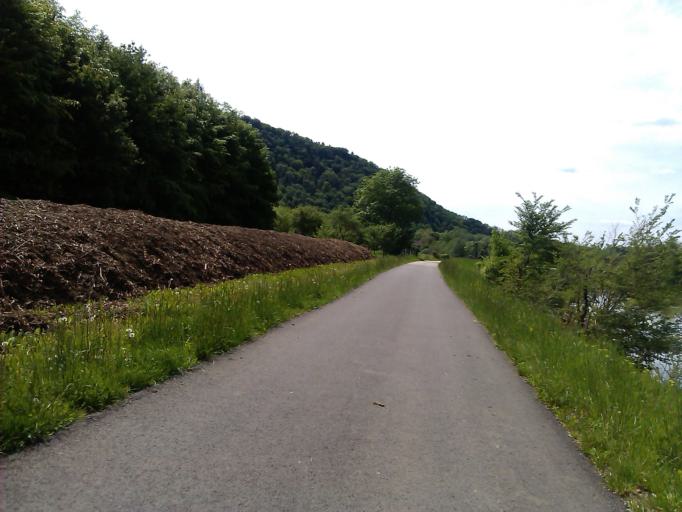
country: FR
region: Franche-Comte
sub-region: Departement du Doubs
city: Montferrand-le-Chateau
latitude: 47.1707
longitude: 5.9216
